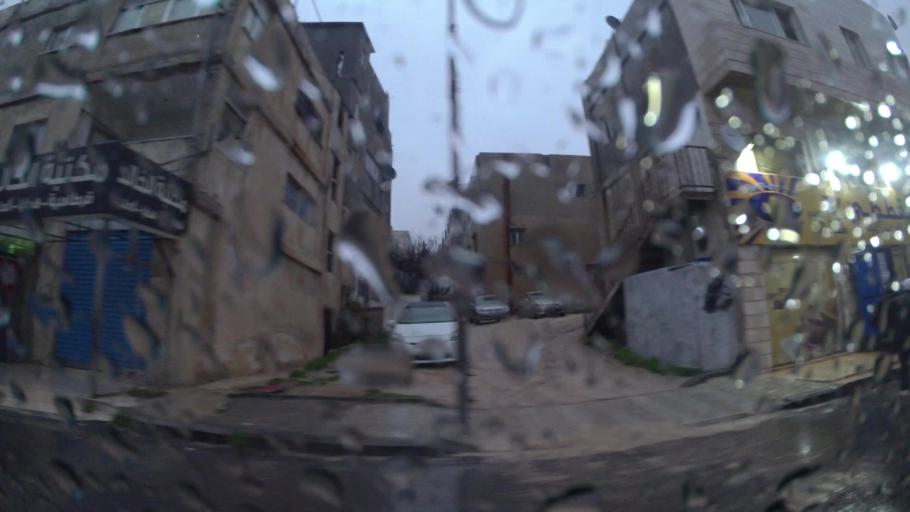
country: JO
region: Amman
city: Al Jubayhah
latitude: 32.0256
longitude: 35.8452
